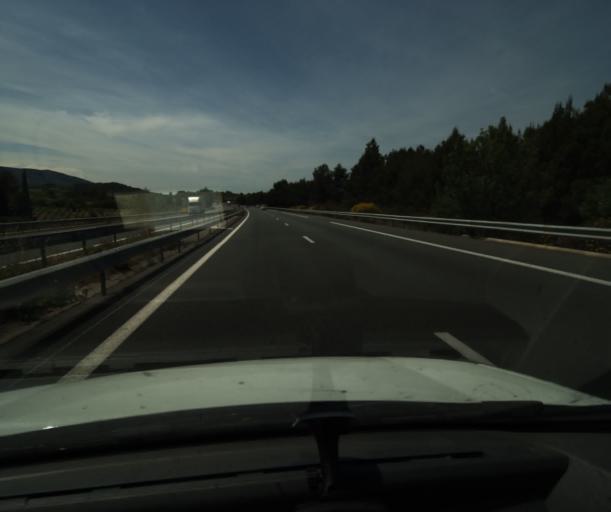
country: FR
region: Languedoc-Roussillon
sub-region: Departement de l'Aude
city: Capendu
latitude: 43.1787
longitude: 2.5900
